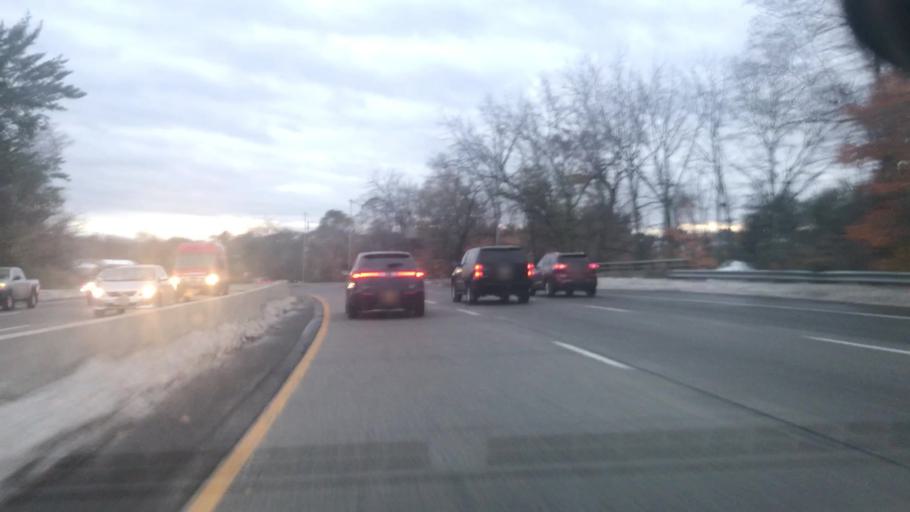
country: US
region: New Jersey
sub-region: Bergen County
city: Lyndhurst
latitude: 40.8195
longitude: -74.1356
